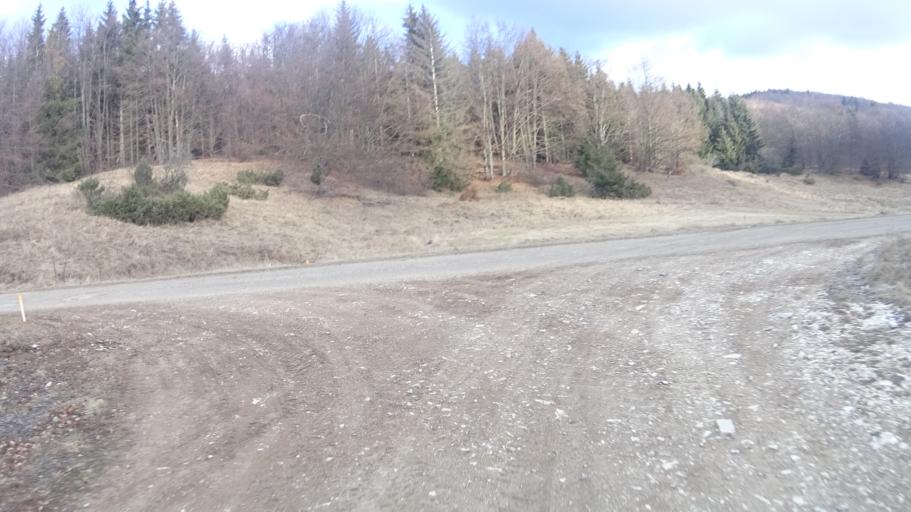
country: HU
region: Heves
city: Szilvasvarad
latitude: 48.0773
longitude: 20.4508
